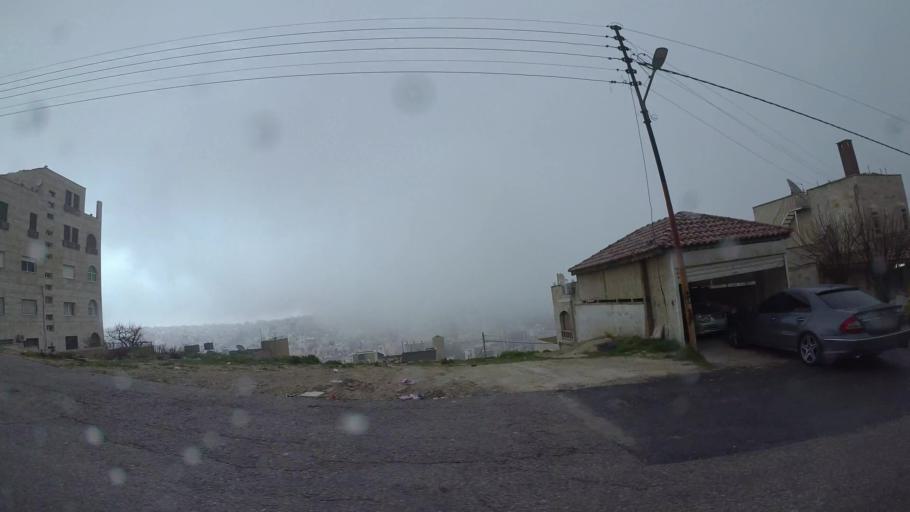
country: JO
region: Amman
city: Al Jubayhah
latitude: 32.0187
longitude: 35.8401
